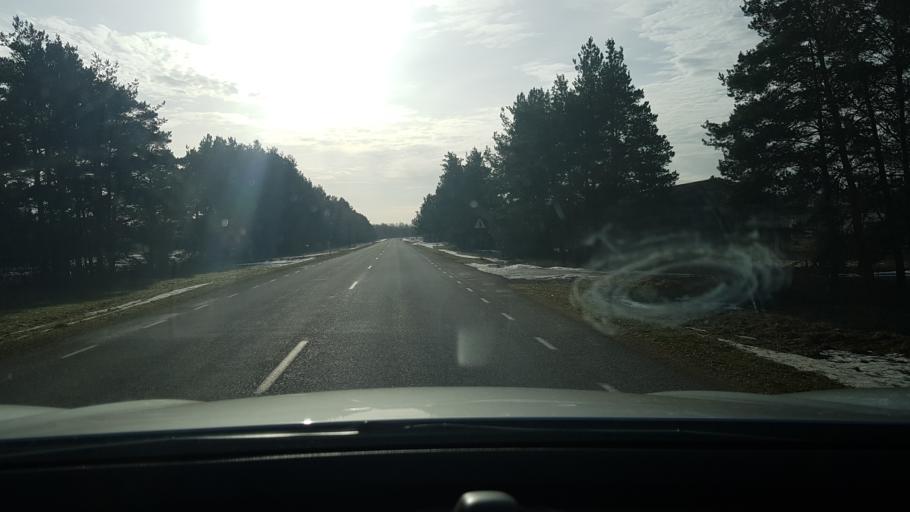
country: EE
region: Saare
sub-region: Kuressaare linn
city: Kuressaare
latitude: 58.5159
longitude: 22.7041
